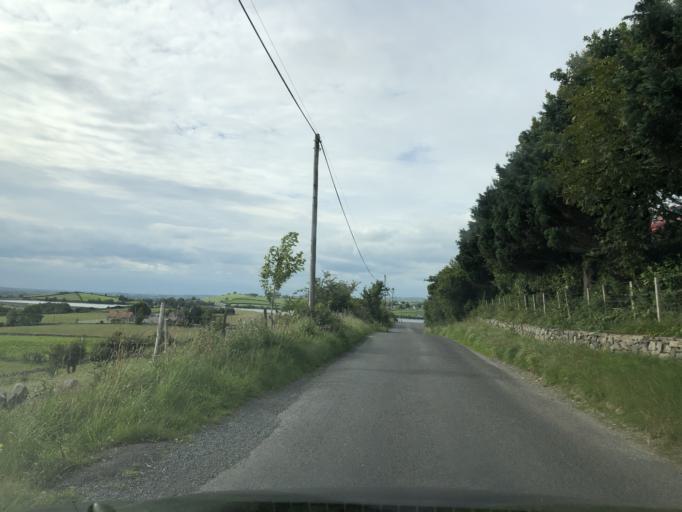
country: GB
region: Northern Ireland
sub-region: Down District
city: Castlewellan
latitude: 54.2317
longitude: -6.0112
